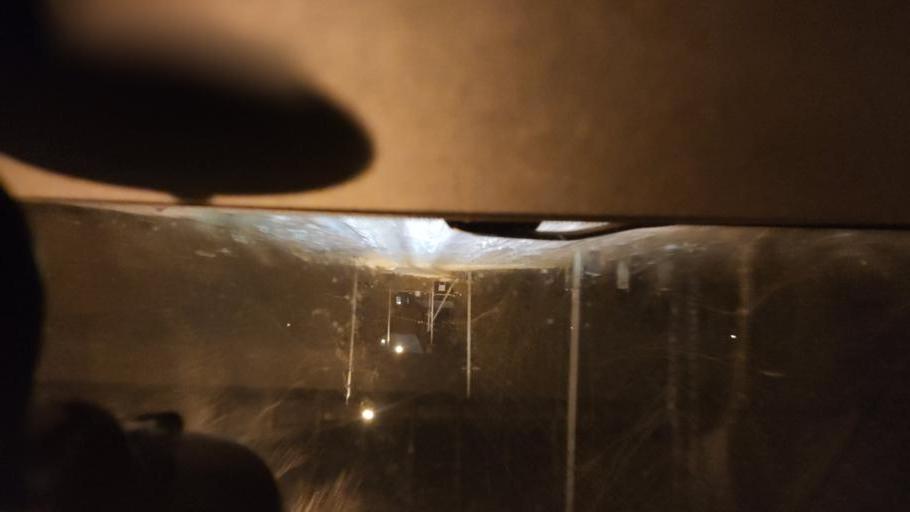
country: RU
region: Perm
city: Perm
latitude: 58.0290
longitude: 56.2228
